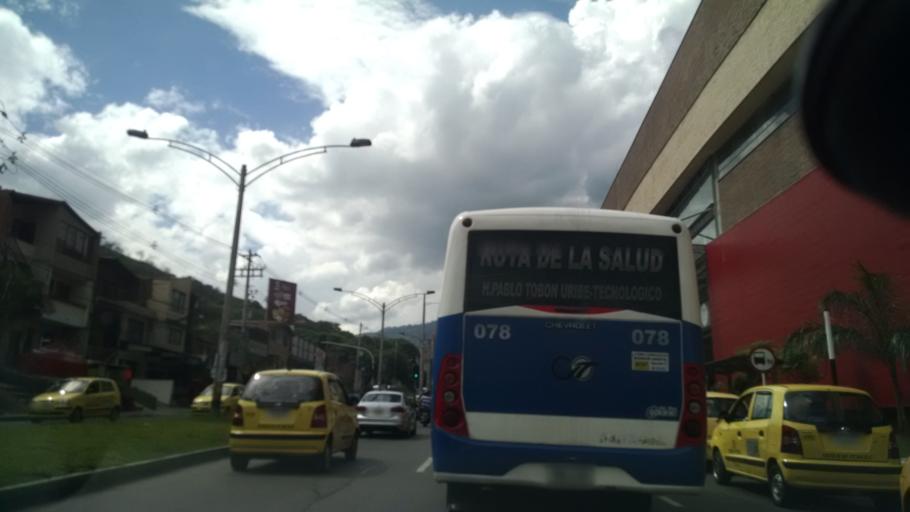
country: CO
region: Antioquia
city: Medellin
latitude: 6.2703
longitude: -75.5769
